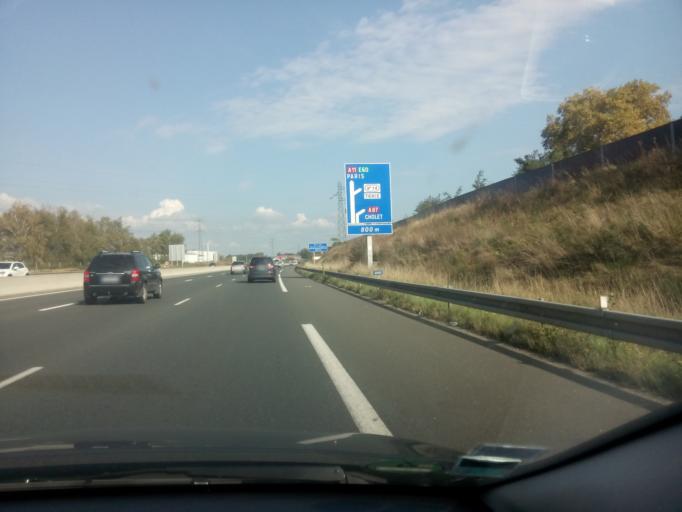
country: FR
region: Pays de la Loire
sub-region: Departement de Maine-et-Loire
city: Ecouflant
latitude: 47.4983
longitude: -0.5179
